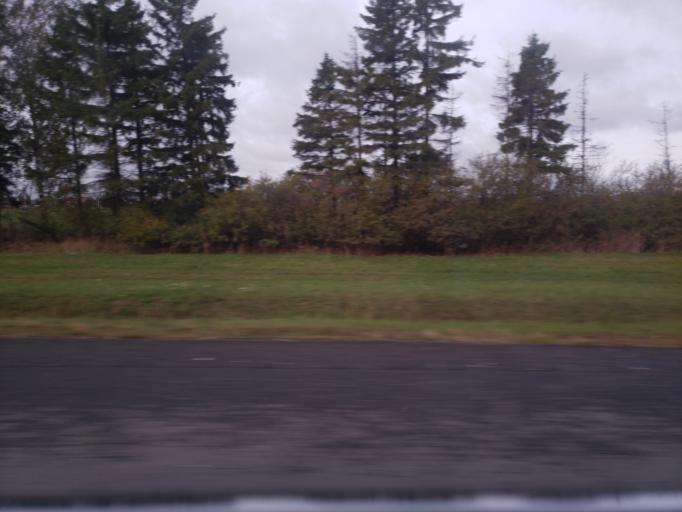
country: RU
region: Moskovskaya
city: Gorki-Leninskiye
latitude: 55.4751
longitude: 37.8526
